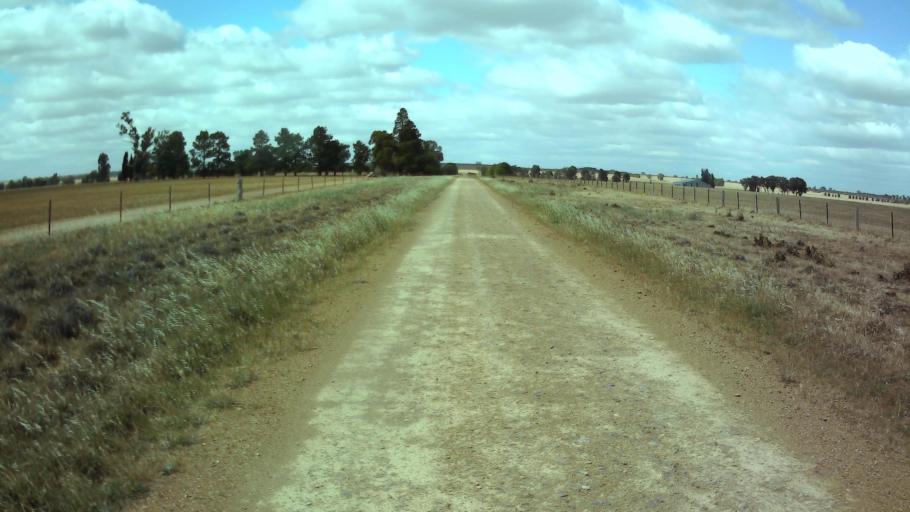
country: AU
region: New South Wales
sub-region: Weddin
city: Grenfell
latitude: -34.0576
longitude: 148.3308
